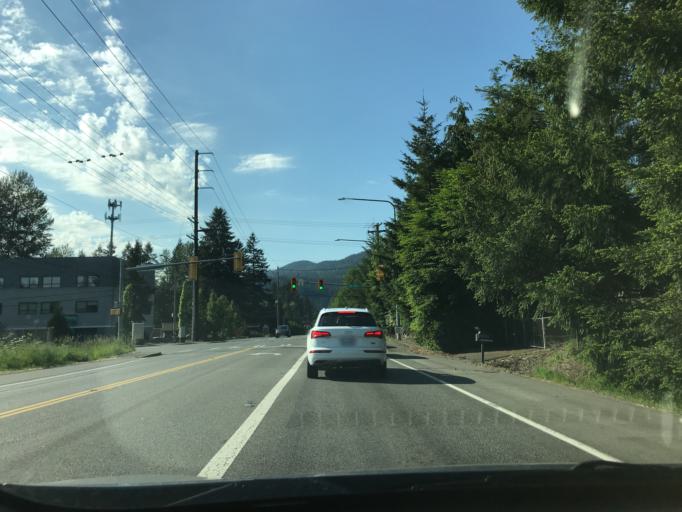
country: US
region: Washington
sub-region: King County
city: Mirrormont
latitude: 47.4722
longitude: -122.0228
